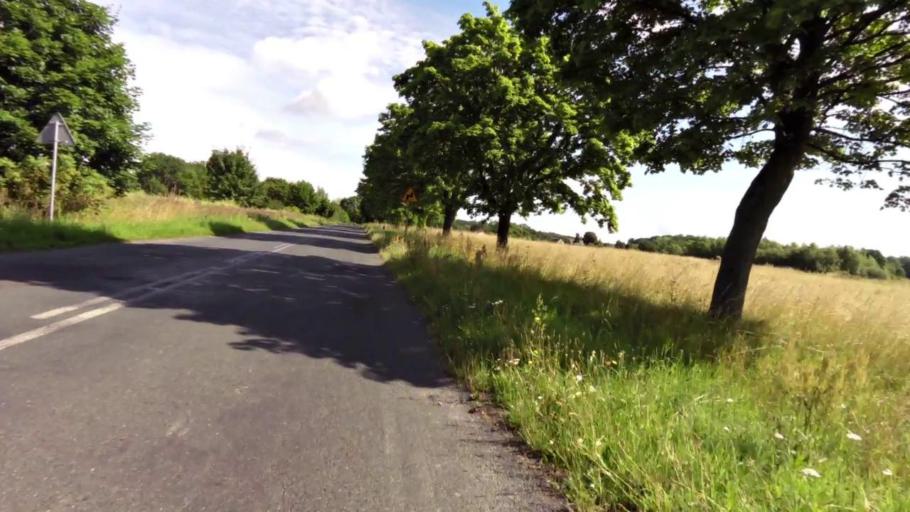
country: PL
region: West Pomeranian Voivodeship
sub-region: Powiat stargardzki
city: Dobrzany
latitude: 53.3761
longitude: 15.4352
